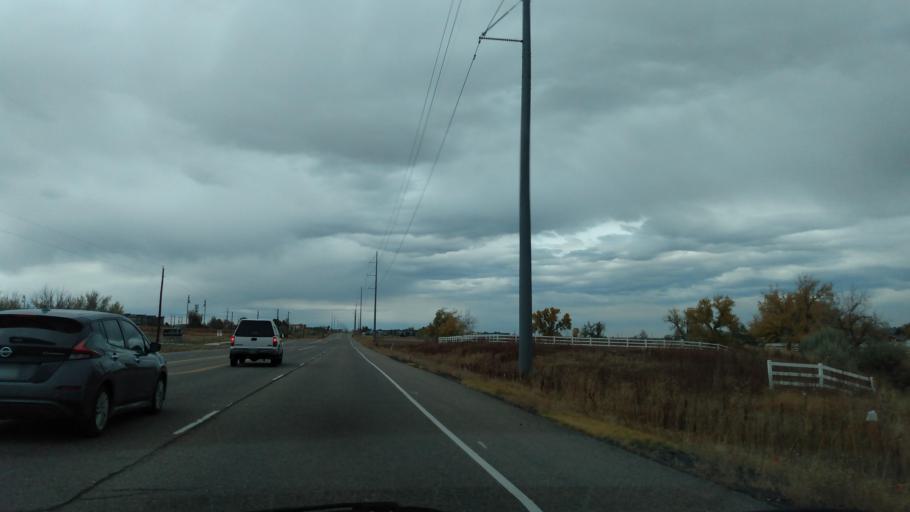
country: US
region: Colorado
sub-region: Adams County
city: Northglenn
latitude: 39.9479
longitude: -104.9782
